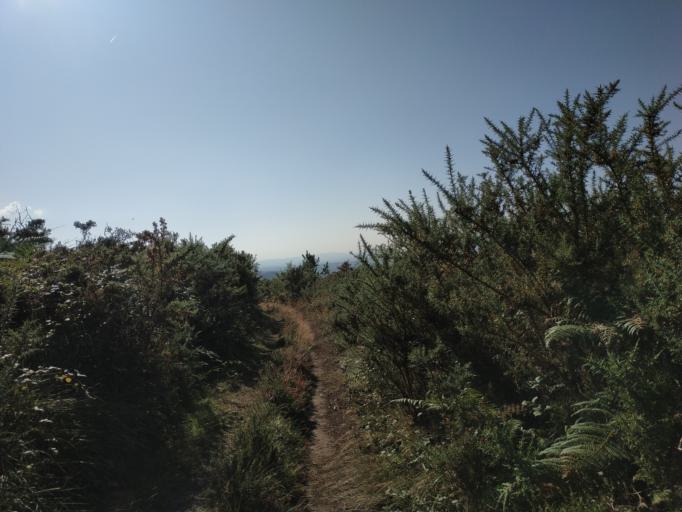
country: ES
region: Galicia
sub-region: Provincia da Coruna
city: Laracha
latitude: 43.2294
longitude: -8.5372
